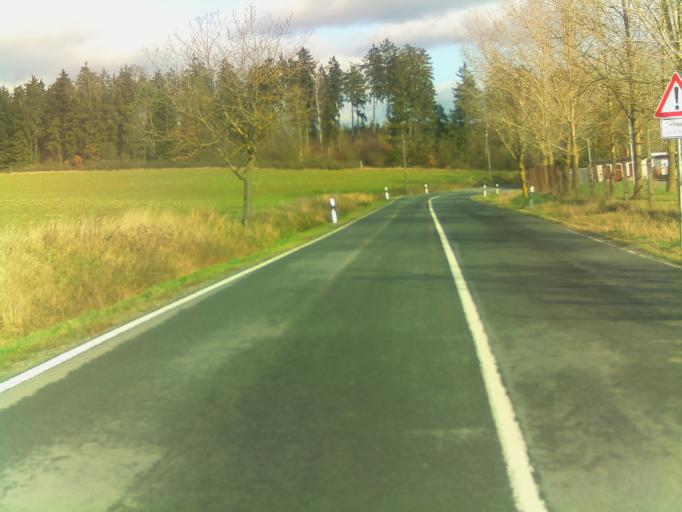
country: DE
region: Thuringia
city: Reurieth
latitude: 50.4049
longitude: 10.6717
